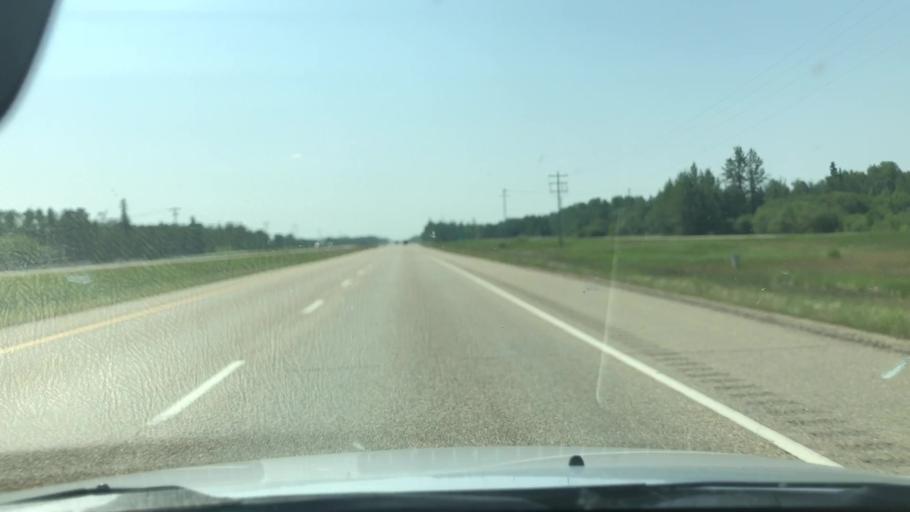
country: CA
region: Alberta
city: Devon
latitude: 53.4392
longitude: -113.7631
